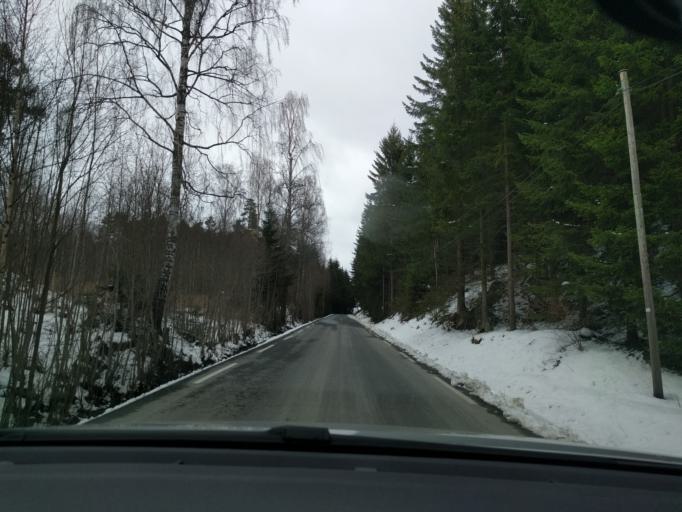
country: NO
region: Hedmark
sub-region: Stange
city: Stange
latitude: 60.6891
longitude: 11.1323
